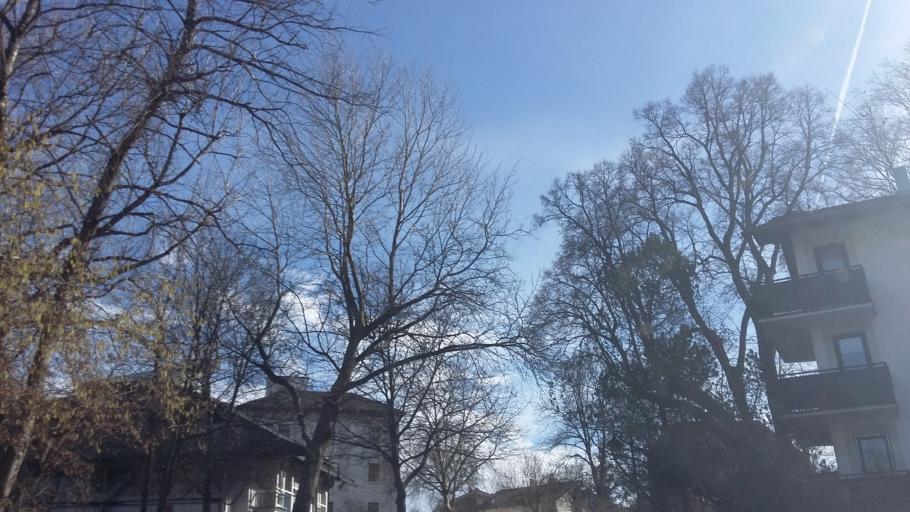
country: DE
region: Bavaria
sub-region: Upper Bavaria
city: Starnberg
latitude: 47.9985
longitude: 11.3357
